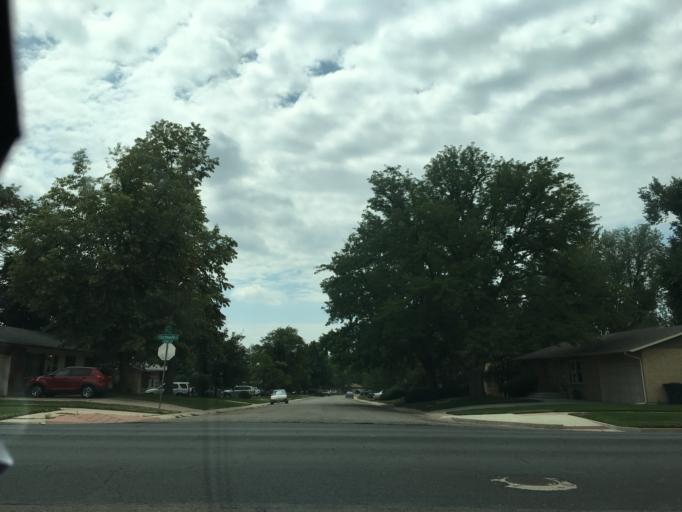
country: US
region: Colorado
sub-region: Arapahoe County
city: Sheridan
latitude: 39.6611
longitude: -105.0392
